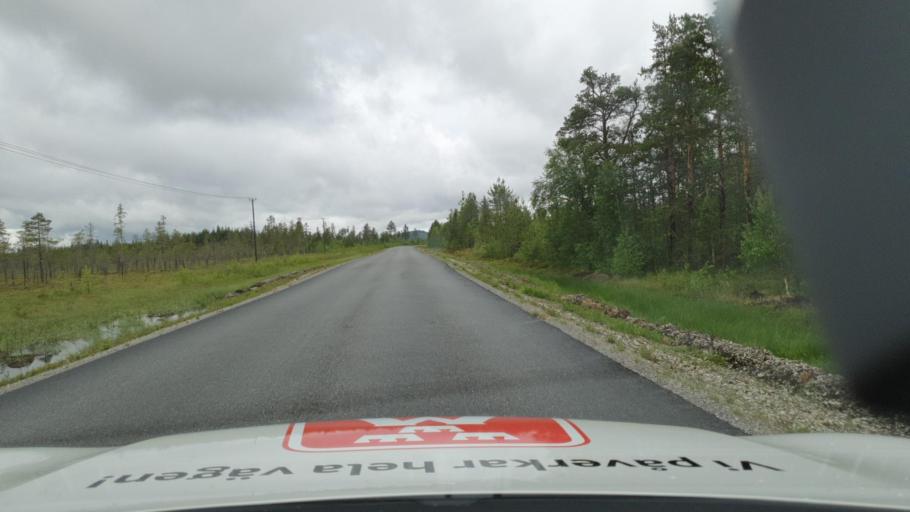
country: SE
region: Vaesterbotten
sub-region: Dorotea Kommun
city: Dorotea
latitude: 64.1279
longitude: 16.6347
